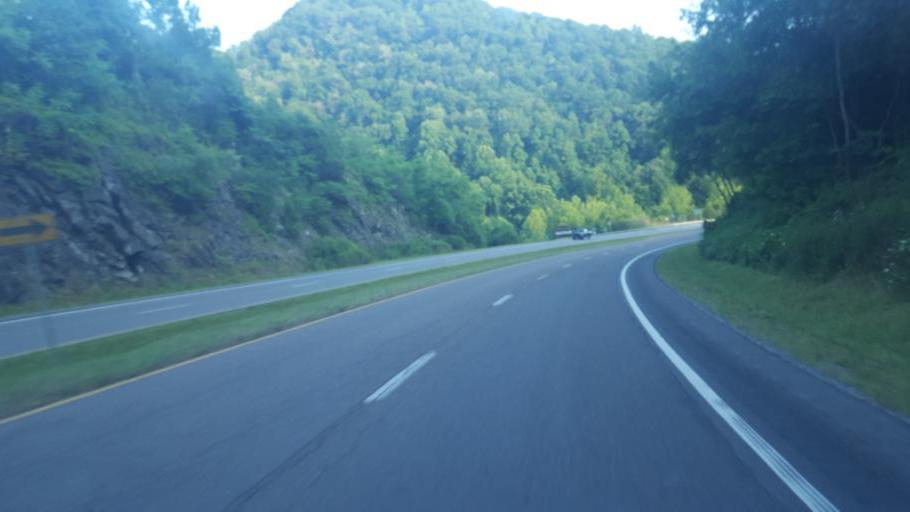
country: US
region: Tennessee
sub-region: Hawkins County
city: Mount Carmel
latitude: 36.6869
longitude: -82.7531
